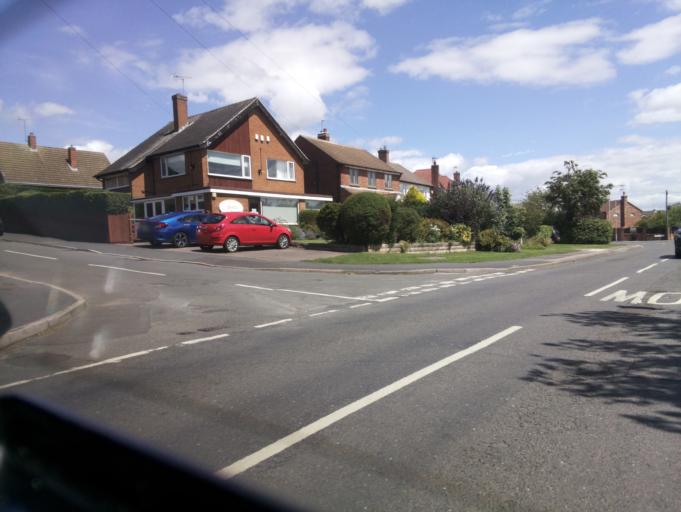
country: GB
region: England
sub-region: Nottinghamshire
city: Cotgrave
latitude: 52.8770
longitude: -1.0875
